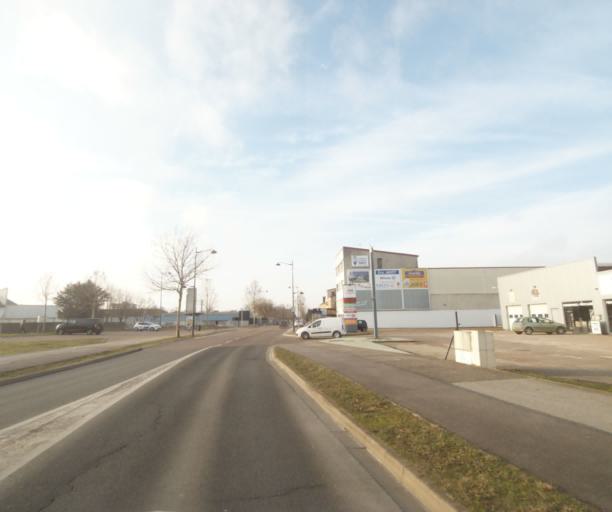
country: FR
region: Champagne-Ardenne
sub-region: Departement de la Haute-Marne
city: Bettancourt-la-Ferree
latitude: 48.6474
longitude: 4.9567
